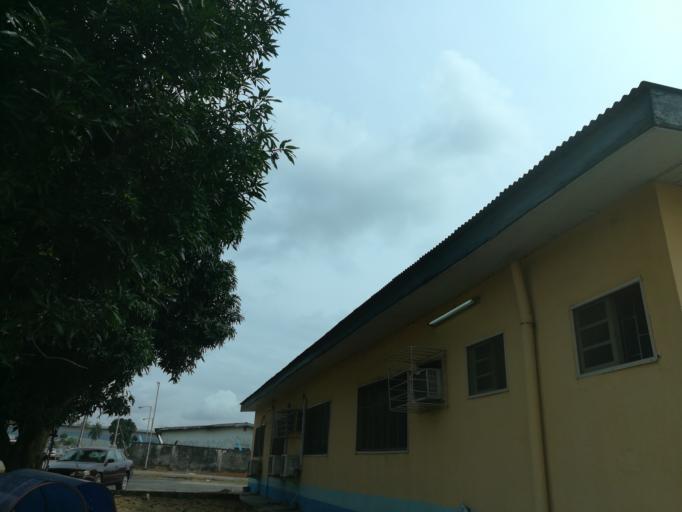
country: NG
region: Lagos
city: Oshodi
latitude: 6.5738
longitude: 3.3247
